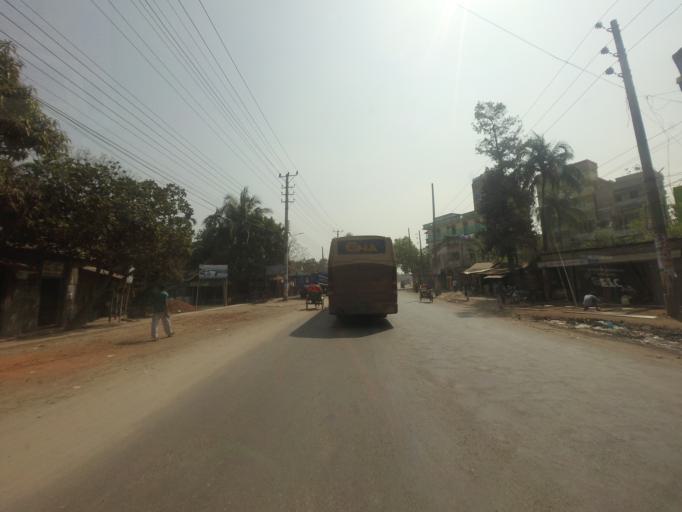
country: BD
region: Dhaka
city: Bhairab Bazar
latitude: 24.0546
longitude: 90.9859
